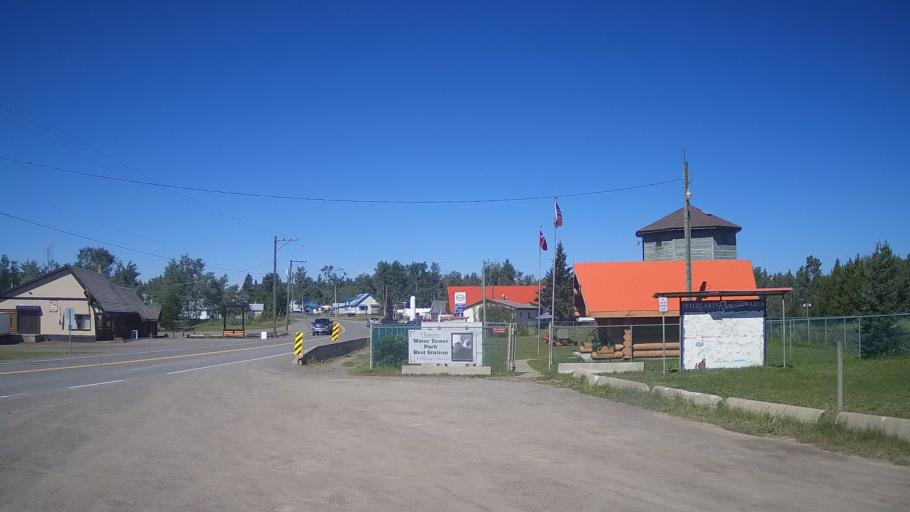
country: CA
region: British Columbia
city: Cache Creek
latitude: 51.5550
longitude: -121.2037
